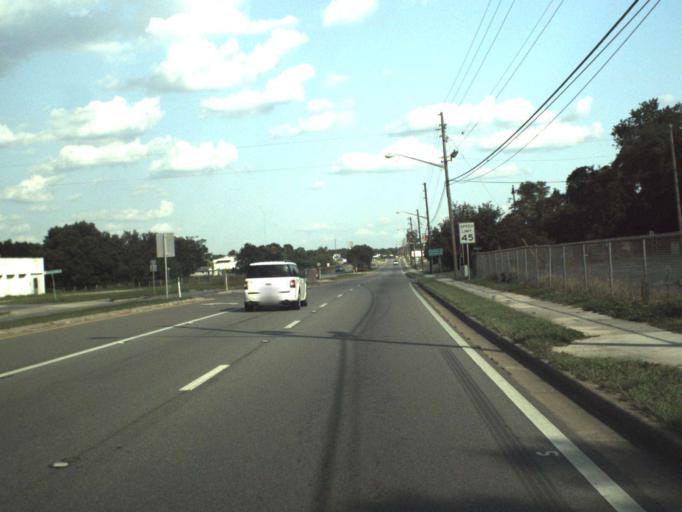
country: US
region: Florida
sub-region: Lake County
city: Mascotte
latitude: 28.5759
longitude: -81.8831
